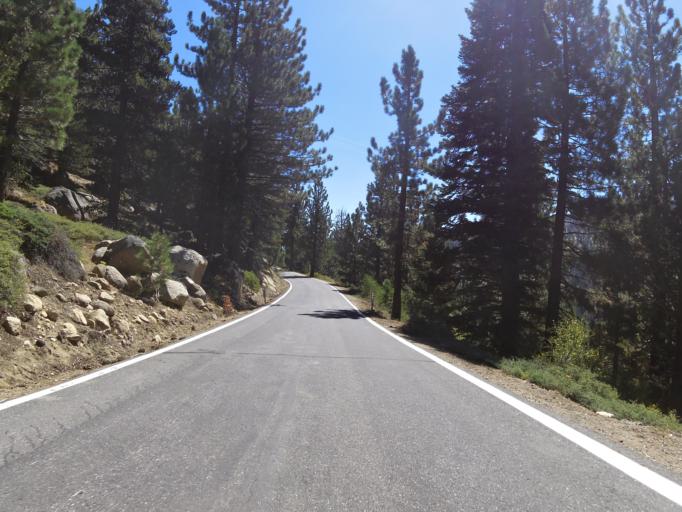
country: US
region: Nevada
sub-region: Douglas County
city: Gardnerville Ranchos
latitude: 38.5500
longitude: -119.8485
